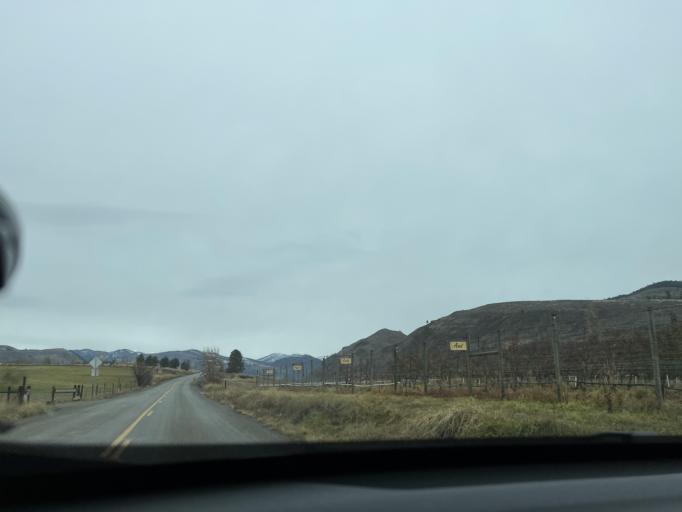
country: US
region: Washington
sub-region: Okanogan County
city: Brewster
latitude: 48.5100
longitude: -120.1733
